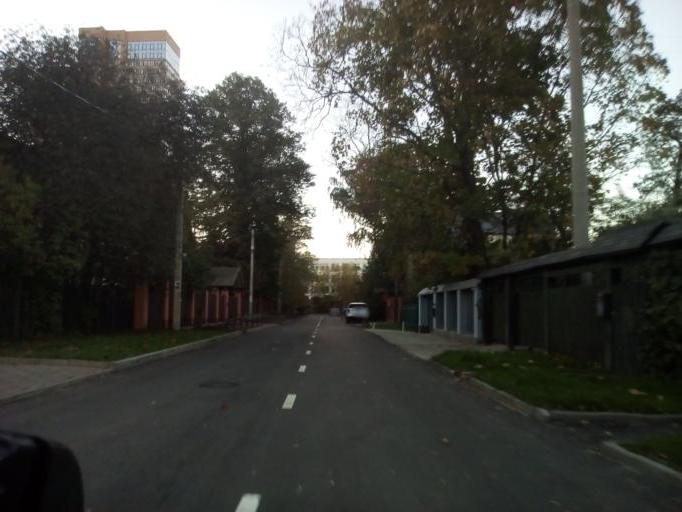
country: RU
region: Moscow
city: Sokol
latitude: 55.8043
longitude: 37.5023
